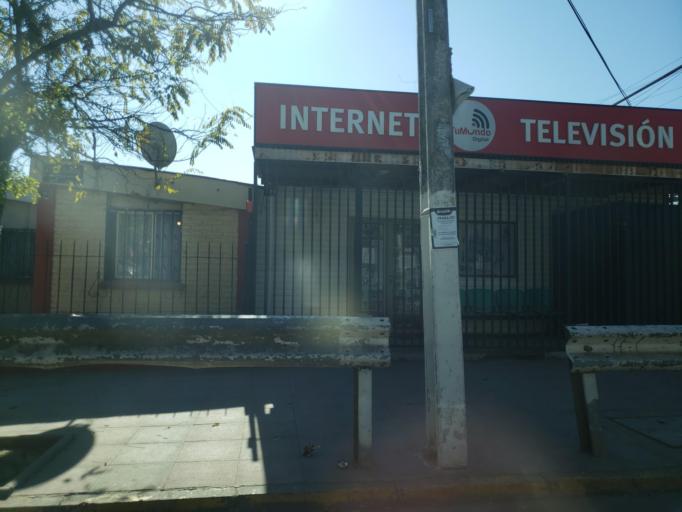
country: CL
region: Santiago Metropolitan
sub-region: Provincia de Talagante
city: El Monte
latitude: -33.6776
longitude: -70.9785
